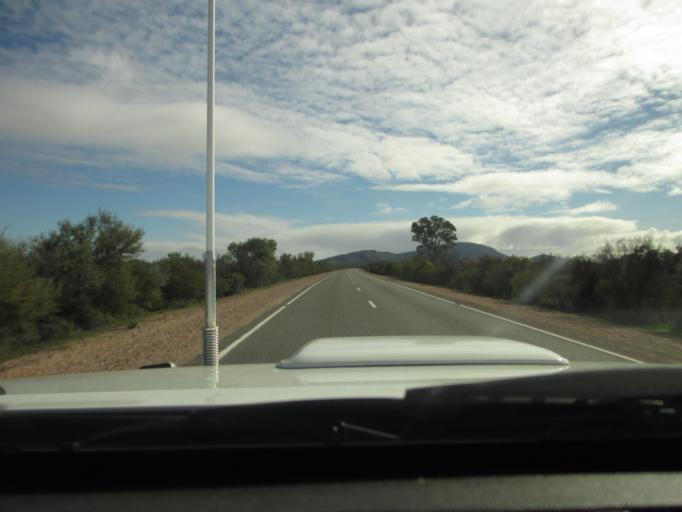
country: AU
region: South Australia
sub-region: Flinders Ranges
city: Quorn
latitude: -31.8303
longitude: 138.3849
